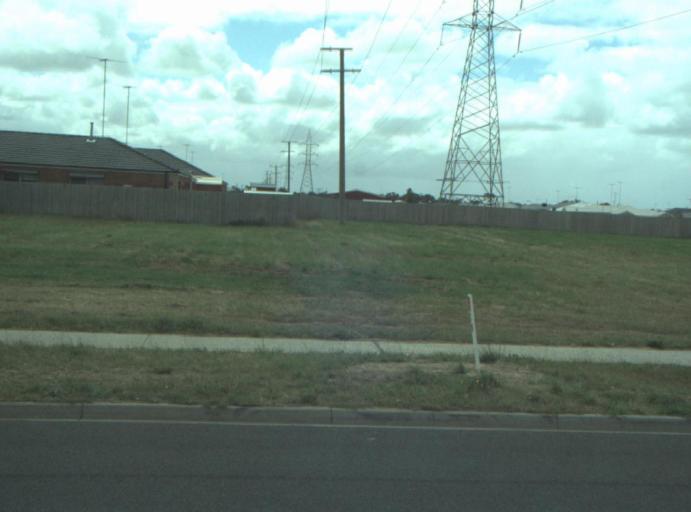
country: AU
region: Victoria
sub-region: Greater Geelong
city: Breakwater
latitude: -38.1989
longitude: 144.3473
